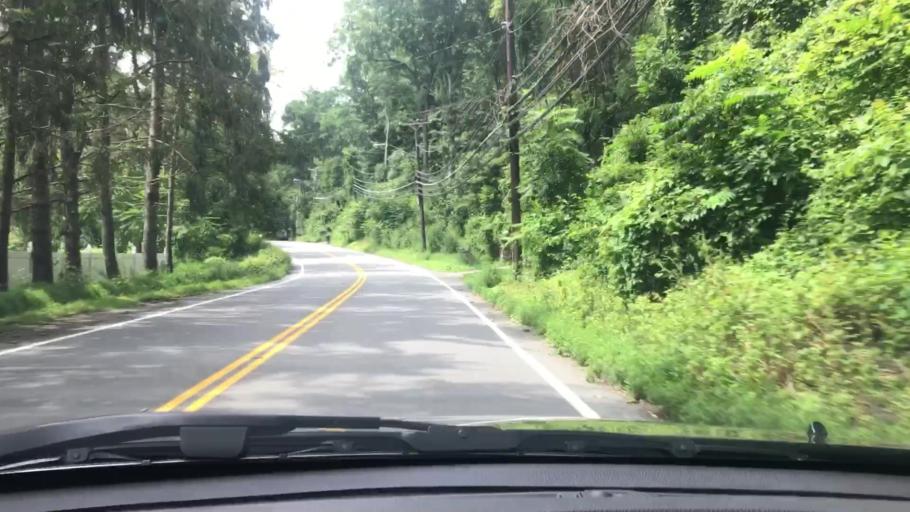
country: US
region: New York
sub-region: Westchester County
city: Bedford
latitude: 41.2030
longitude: -73.6303
